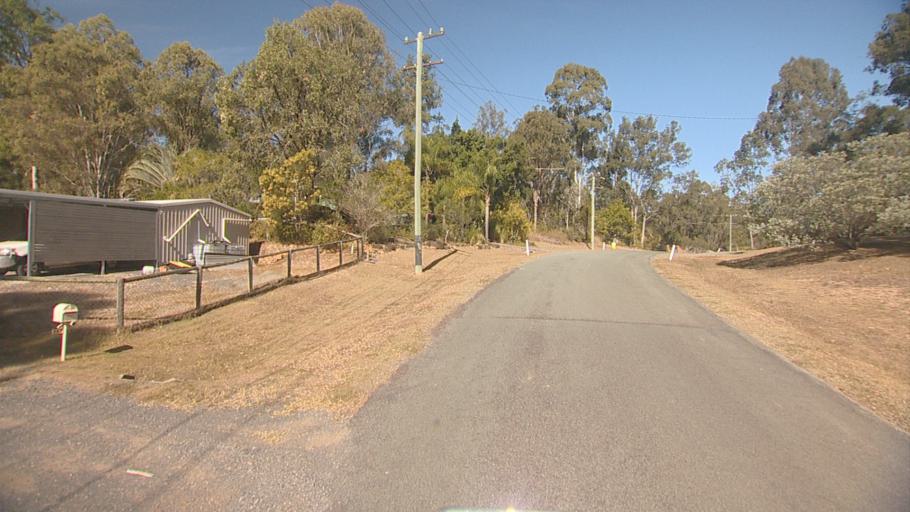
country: AU
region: Queensland
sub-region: Logan
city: Cedar Vale
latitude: -27.8516
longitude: 152.9912
